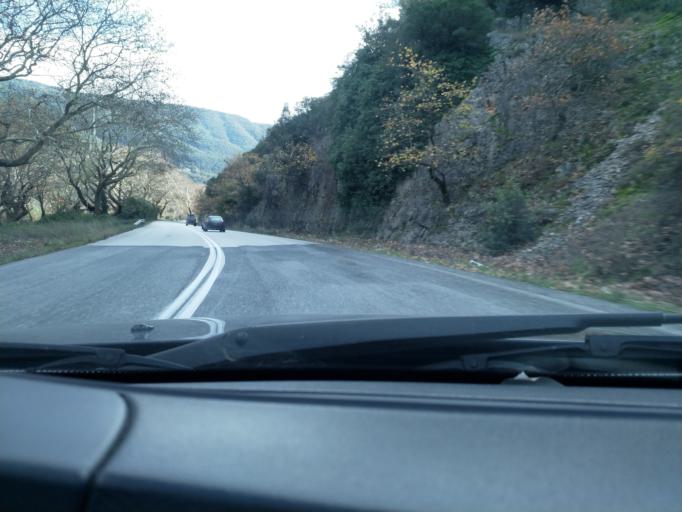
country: GR
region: Epirus
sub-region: Nomos Prevezis
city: Pappadates
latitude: 39.3880
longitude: 20.8631
